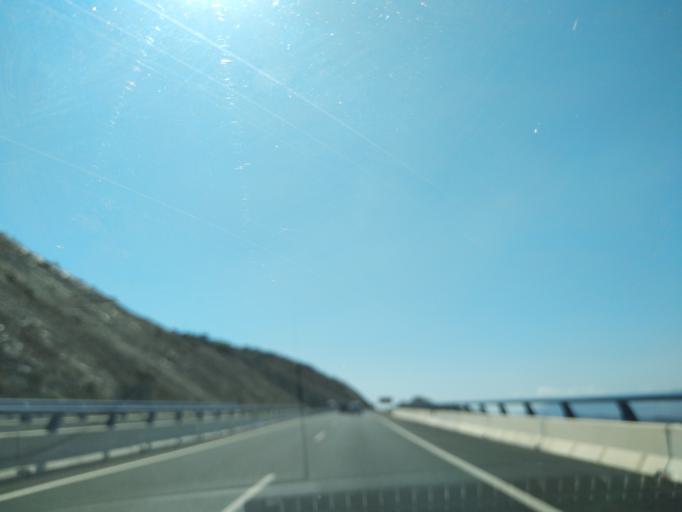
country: ES
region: Andalusia
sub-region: Provincia de Malaga
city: Almogia
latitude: 36.8520
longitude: -4.4846
